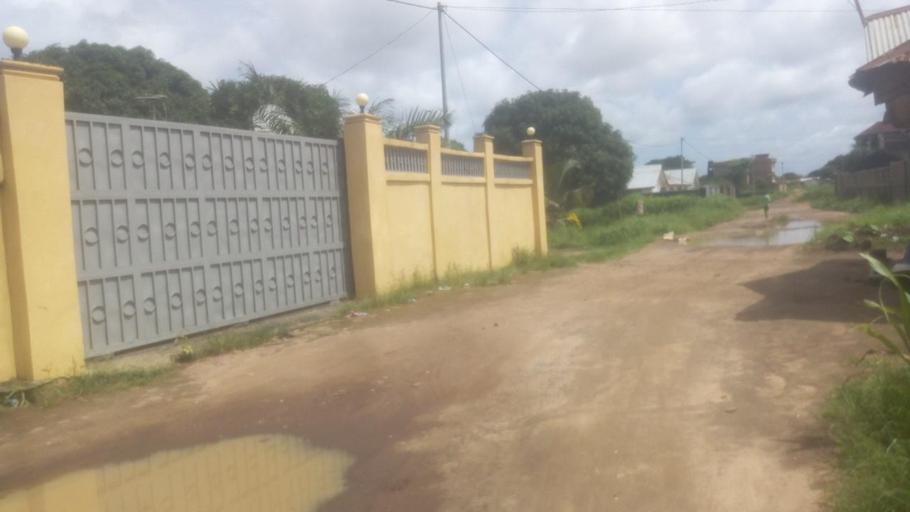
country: SL
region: Northern Province
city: Masoyila
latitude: 8.5985
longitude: -13.1876
